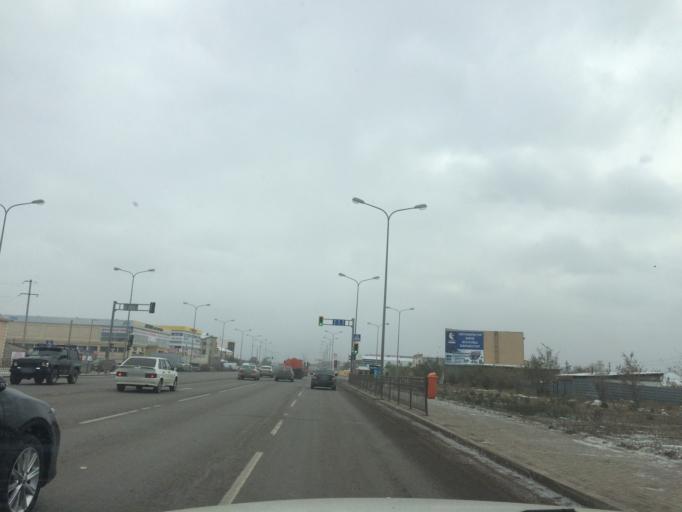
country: KZ
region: Astana Qalasy
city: Astana
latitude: 51.1770
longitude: 71.4734
